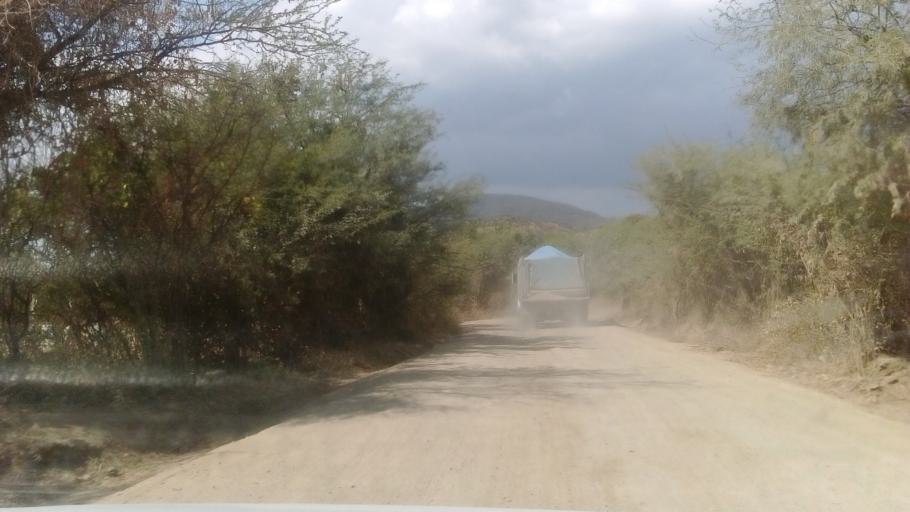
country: MX
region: Guanajuato
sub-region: Silao de la Victoria
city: San Francisco (Banos de Agua Caliente)
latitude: 21.0707
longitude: -101.4610
